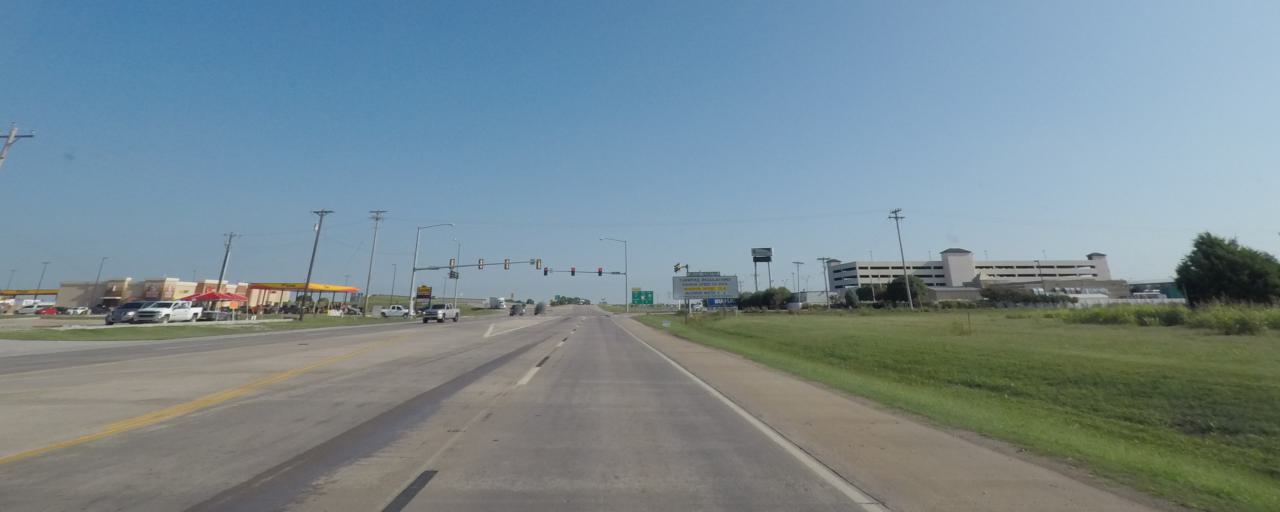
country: US
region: Oklahoma
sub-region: McClain County
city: Newcastle
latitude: 35.2755
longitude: -97.6001
